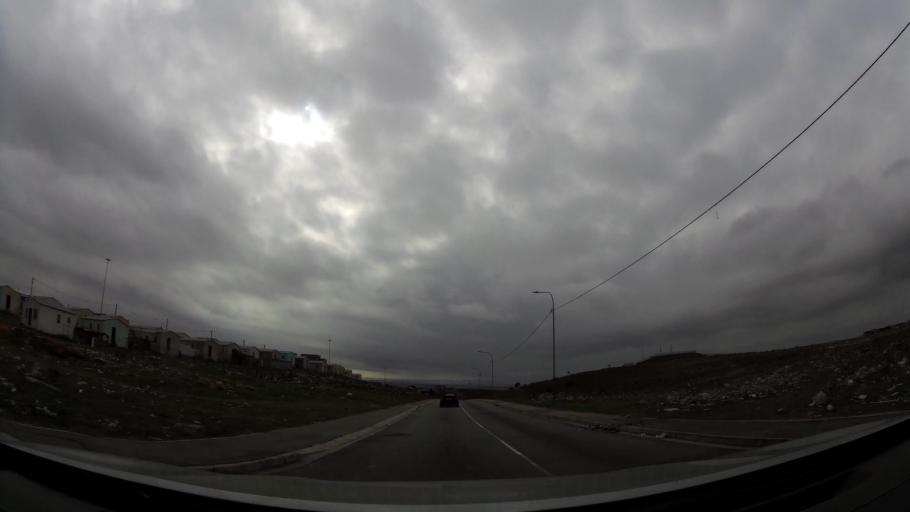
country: ZA
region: Eastern Cape
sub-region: Nelson Mandela Bay Metropolitan Municipality
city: Port Elizabeth
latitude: -33.9138
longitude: 25.5363
